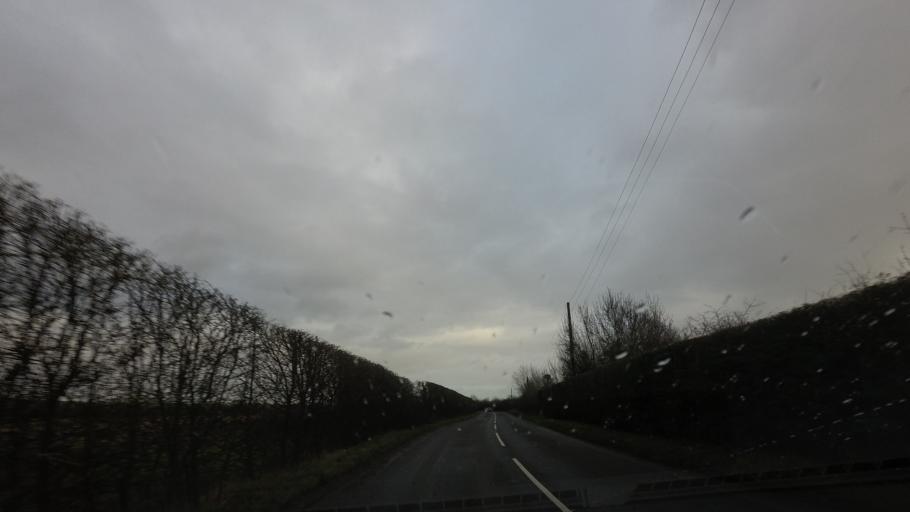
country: GB
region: England
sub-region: Kent
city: Marden
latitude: 51.1862
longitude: 0.4942
